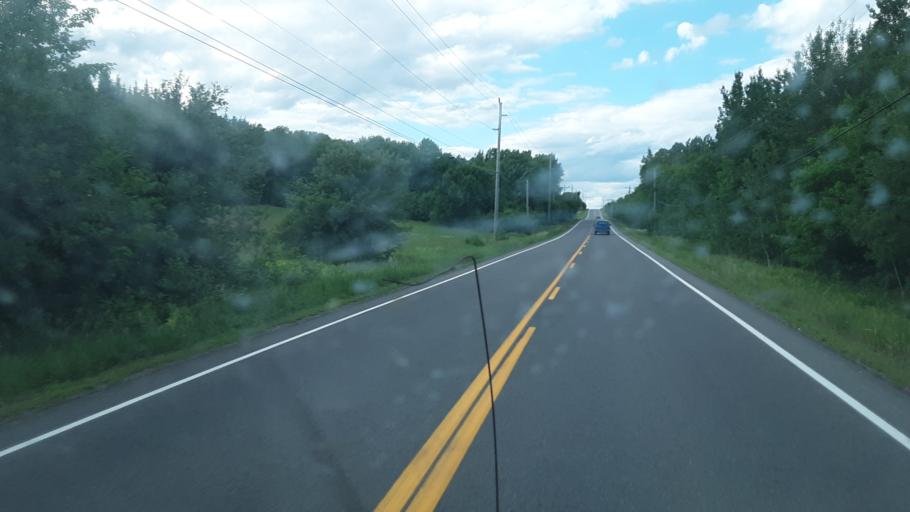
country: US
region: Maine
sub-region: Penobscot County
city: Patten
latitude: 45.9732
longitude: -68.4506
